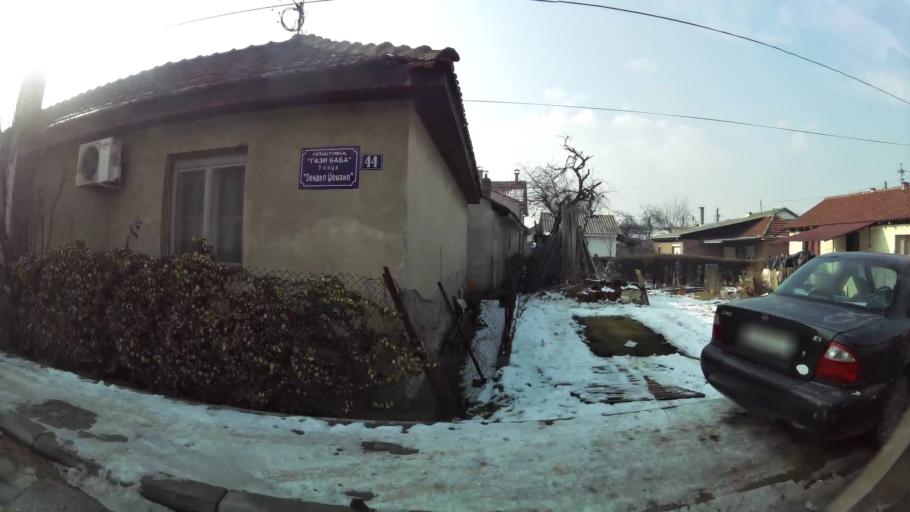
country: MK
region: Kisela Voda
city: Kisela Voda
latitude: 41.9901
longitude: 21.5003
